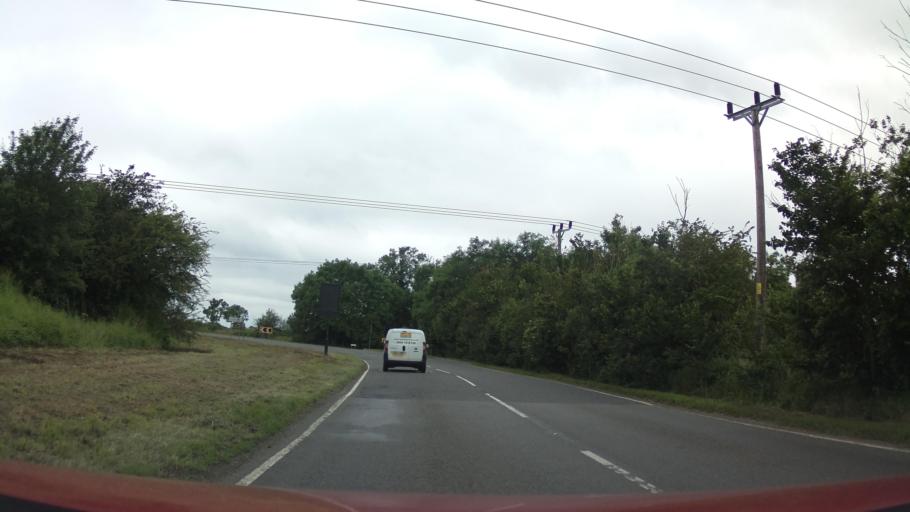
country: GB
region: England
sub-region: Leicestershire
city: Sileby
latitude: 52.8094
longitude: -1.0857
